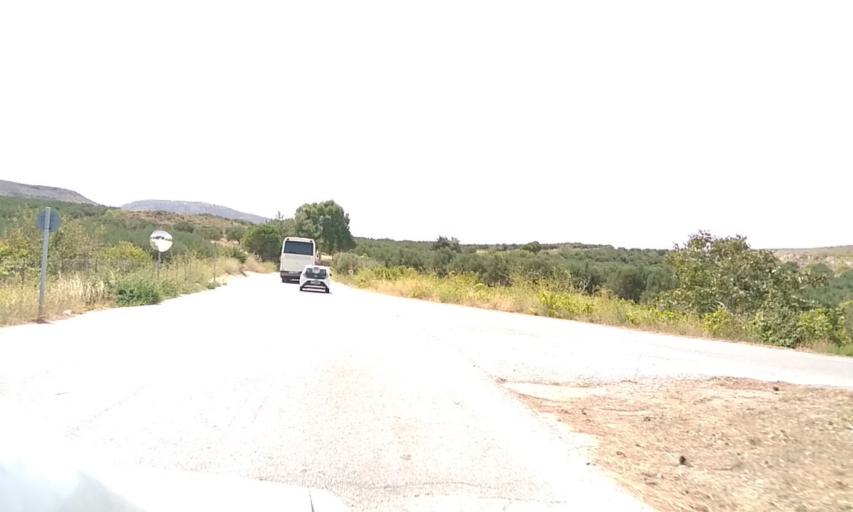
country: GR
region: Crete
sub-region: Nomos Lasithiou
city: Makry-Gialos
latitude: 35.1017
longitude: 26.0601
